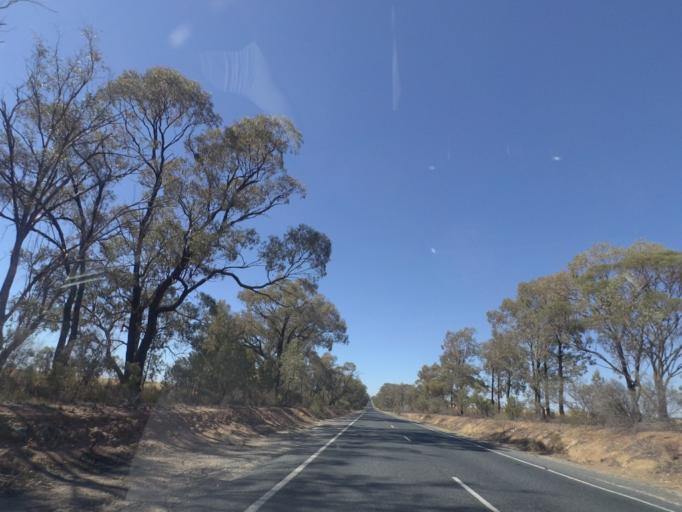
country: AU
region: New South Wales
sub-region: Bland
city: West Wyalong
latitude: -34.1456
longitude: 147.1194
